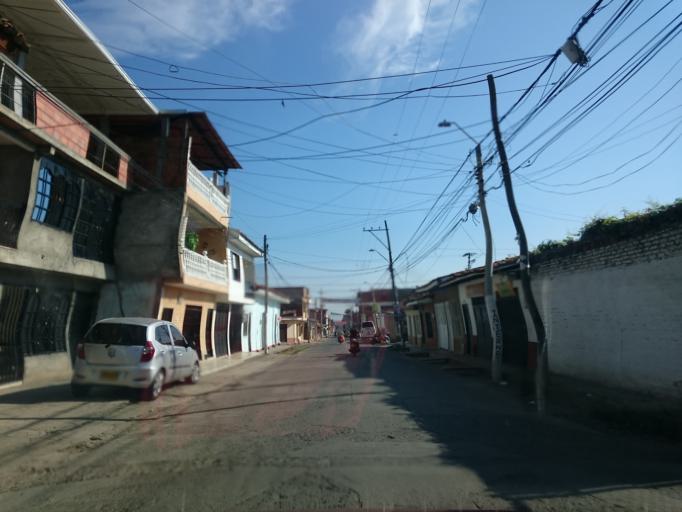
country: CO
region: Cauca
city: Santander de Quilichao
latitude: 3.0133
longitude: -76.4818
